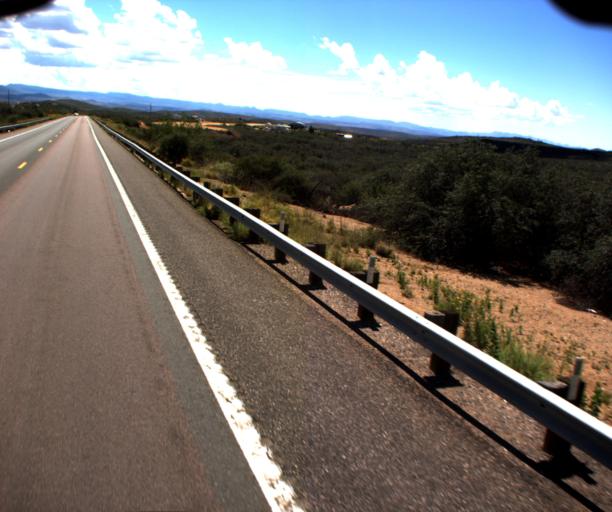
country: US
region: Arizona
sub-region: Yavapai County
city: Dewey-Humboldt
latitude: 34.5402
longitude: -112.1494
